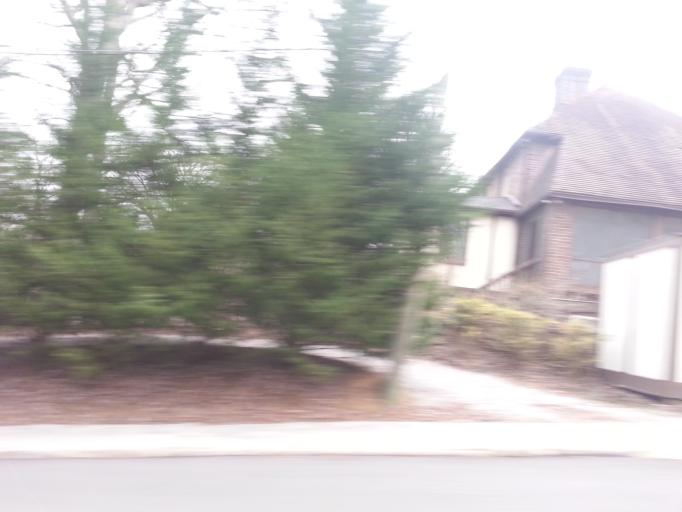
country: US
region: Tennessee
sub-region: Knox County
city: Knoxville
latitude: 35.9445
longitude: -83.9708
